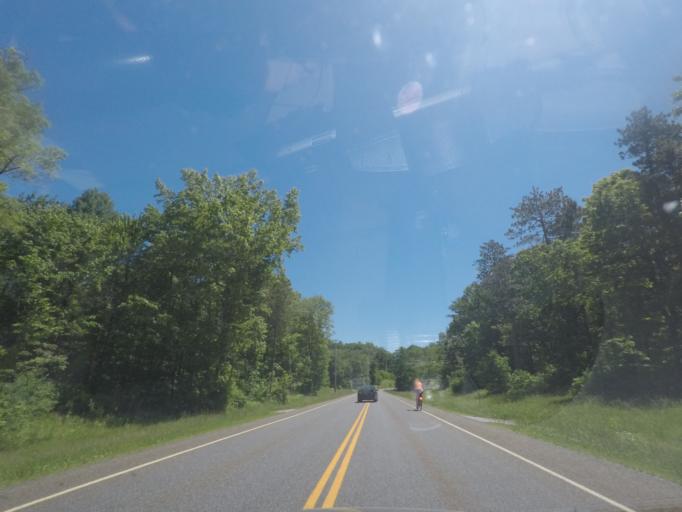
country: US
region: New York
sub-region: Saratoga County
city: Mechanicville
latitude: 42.9472
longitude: -73.7239
